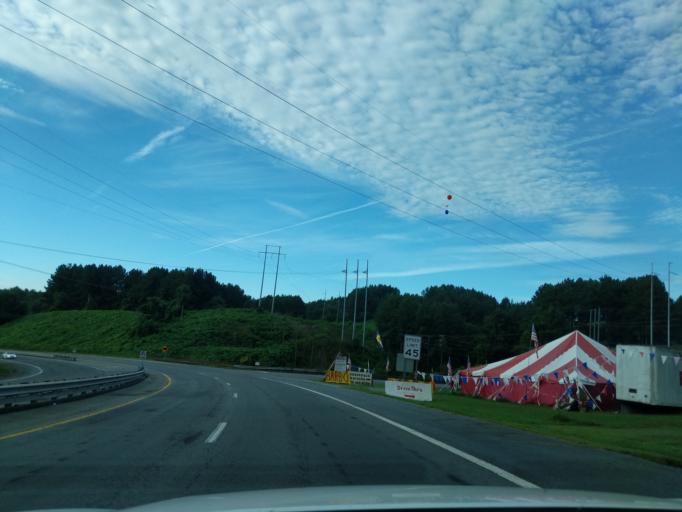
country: US
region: Georgia
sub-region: Fannin County
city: McCaysville
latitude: 35.0046
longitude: -84.3878
